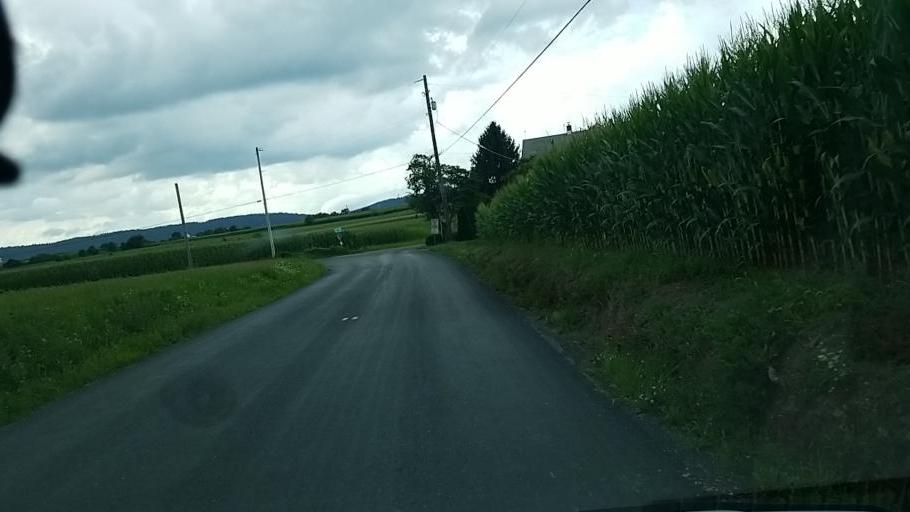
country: US
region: Pennsylvania
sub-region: Dauphin County
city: Elizabethville
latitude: 40.5745
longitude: -76.8388
